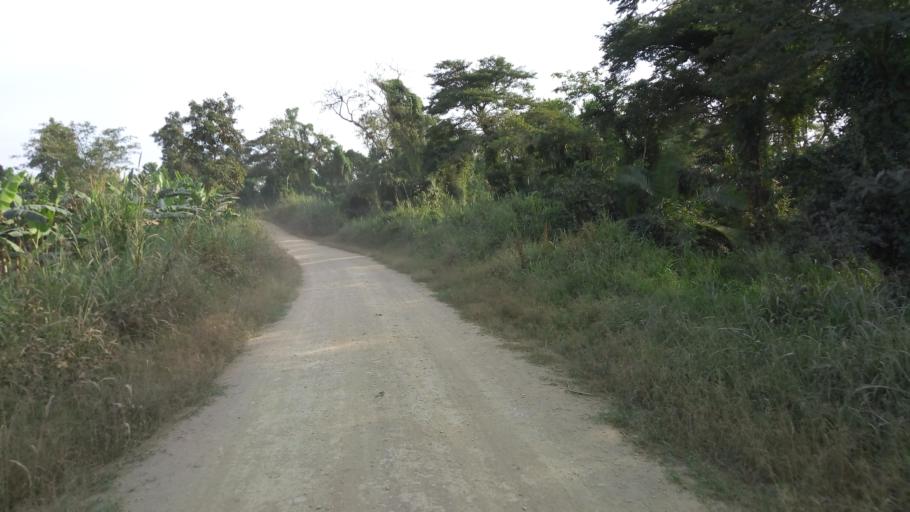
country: UG
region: Central Region
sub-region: Kiboga District
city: Kiboga
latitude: 0.7301
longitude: 31.7318
